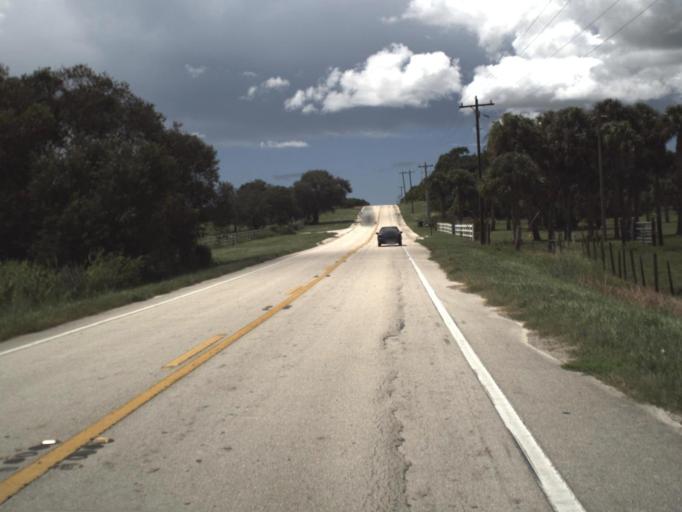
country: US
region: Florida
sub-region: Polk County
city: Fort Meade
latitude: 27.7335
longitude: -81.6881
